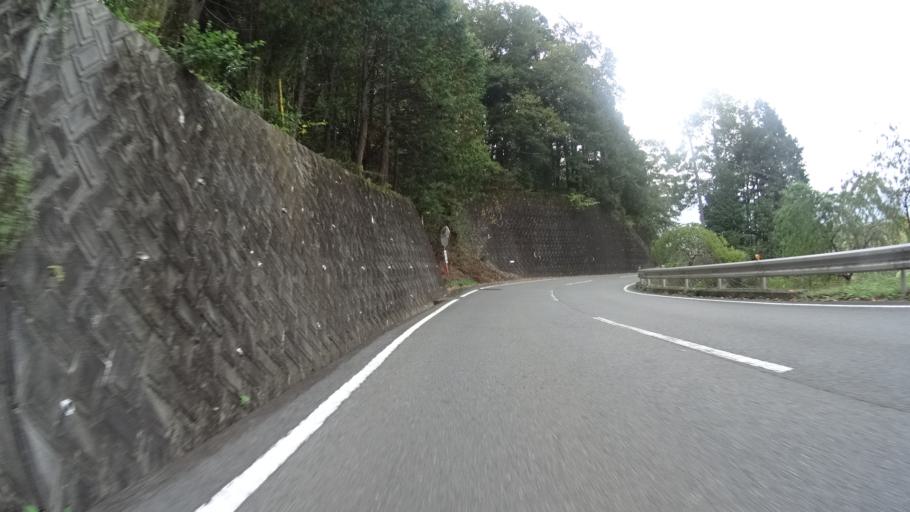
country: JP
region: Yamanashi
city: Otsuki
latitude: 35.6198
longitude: 139.0187
